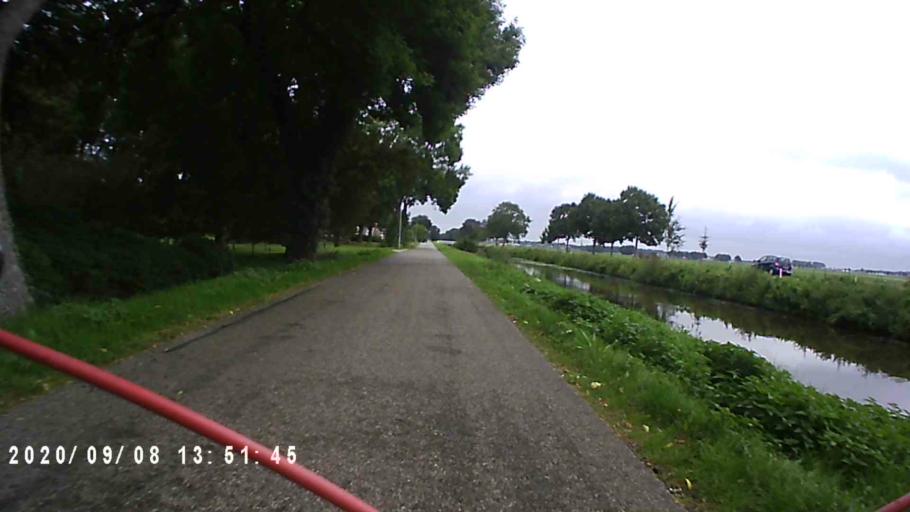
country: NL
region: Groningen
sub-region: Gemeente Veendam
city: Veendam
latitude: 53.1427
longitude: 6.8669
